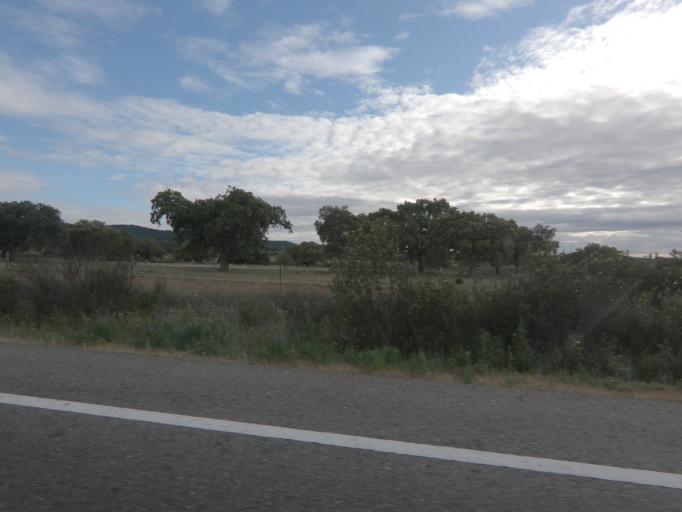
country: ES
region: Extremadura
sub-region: Provincia de Caceres
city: Pedroso de Acim
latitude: 39.8567
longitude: -6.4242
